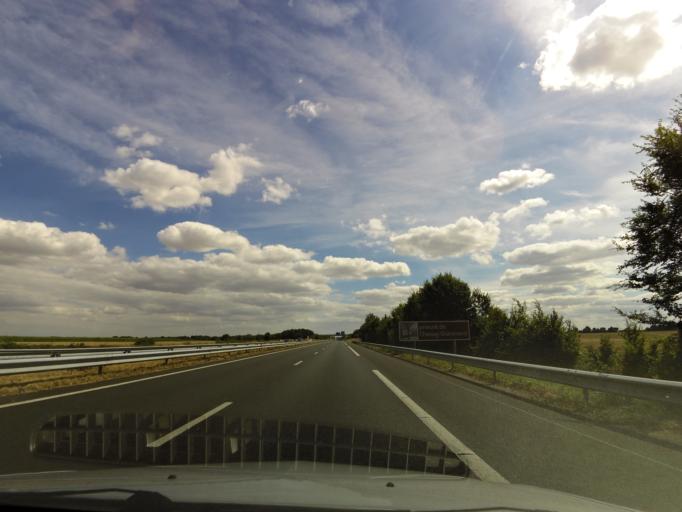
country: FR
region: Pays de la Loire
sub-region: Departement de la Vendee
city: Chauche
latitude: 46.8274
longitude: -1.2226
